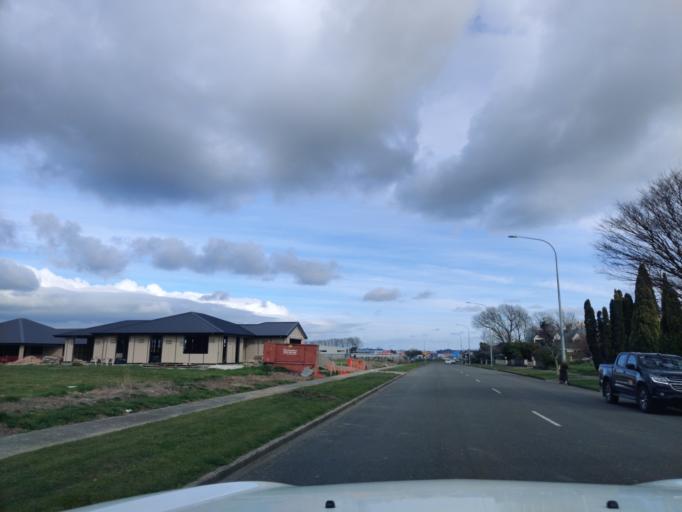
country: NZ
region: Manawatu-Wanganui
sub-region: Palmerston North City
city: Palmerston North
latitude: -40.3369
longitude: 175.6050
